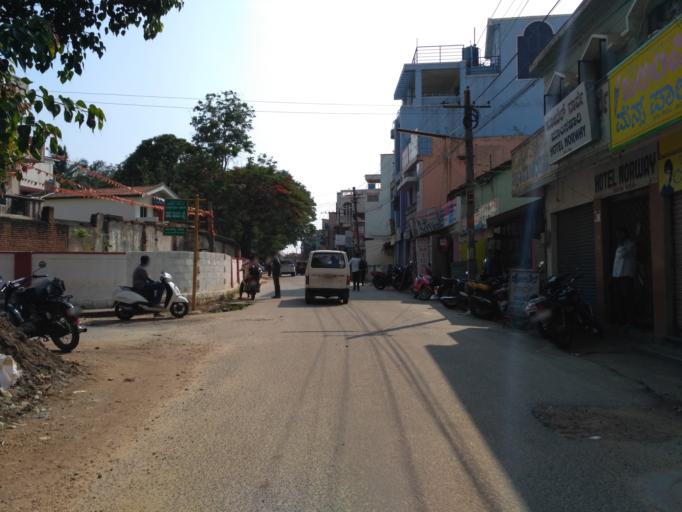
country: IN
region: Karnataka
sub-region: Hassan
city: Hassan
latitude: 13.0107
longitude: 76.1051
